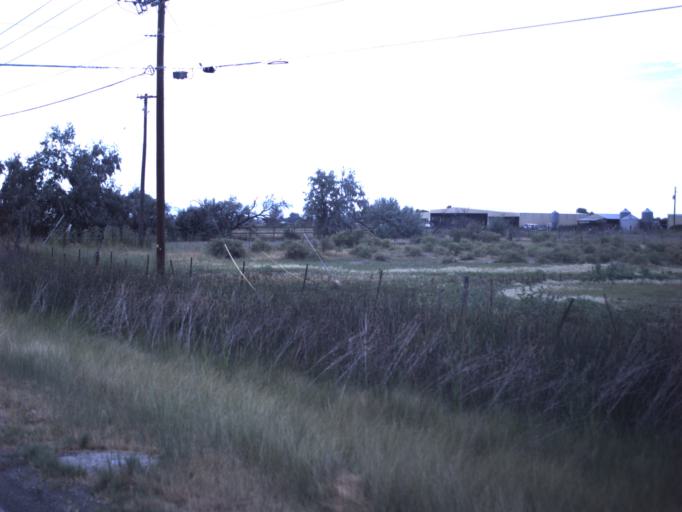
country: US
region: Utah
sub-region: Weber County
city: Hooper
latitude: 41.1399
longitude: -112.1123
